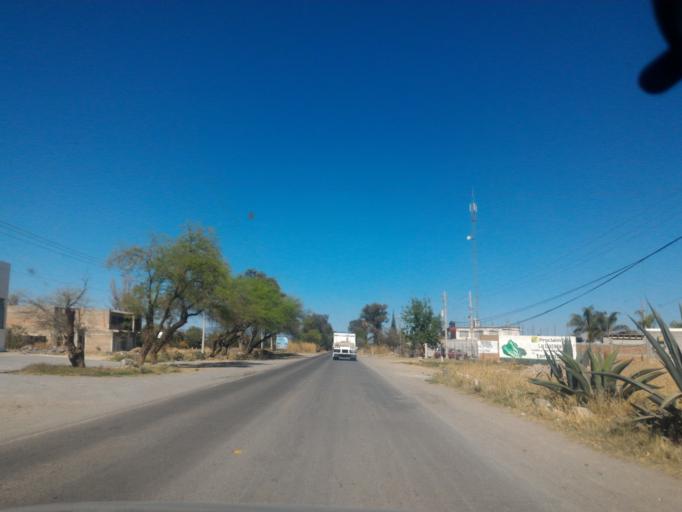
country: MX
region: Guanajuato
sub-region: Leon
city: Malagana (San Antonio del Monte)
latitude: 21.0430
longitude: -101.7640
